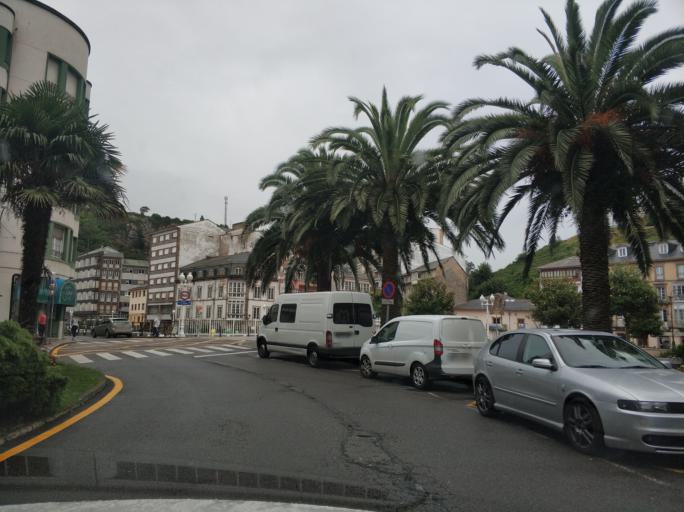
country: ES
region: Asturias
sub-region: Province of Asturias
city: Navia
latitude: 43.5446
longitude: -6.5358
